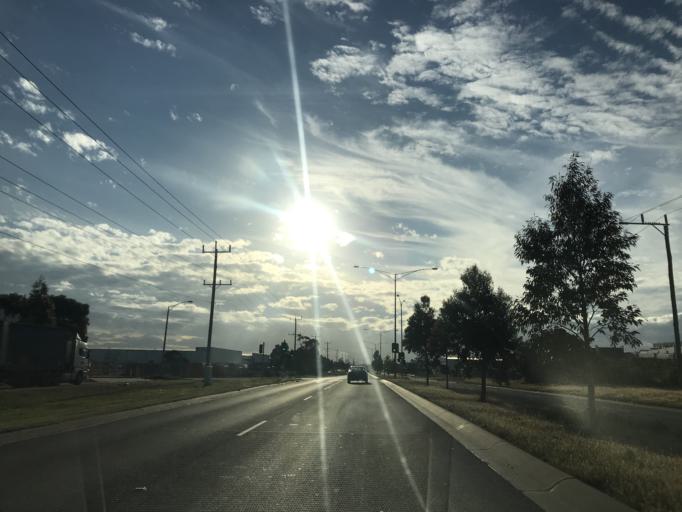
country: AU
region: Victoria
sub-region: Brimbank
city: Derrimut
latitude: -37.8126
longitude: 144.7768
